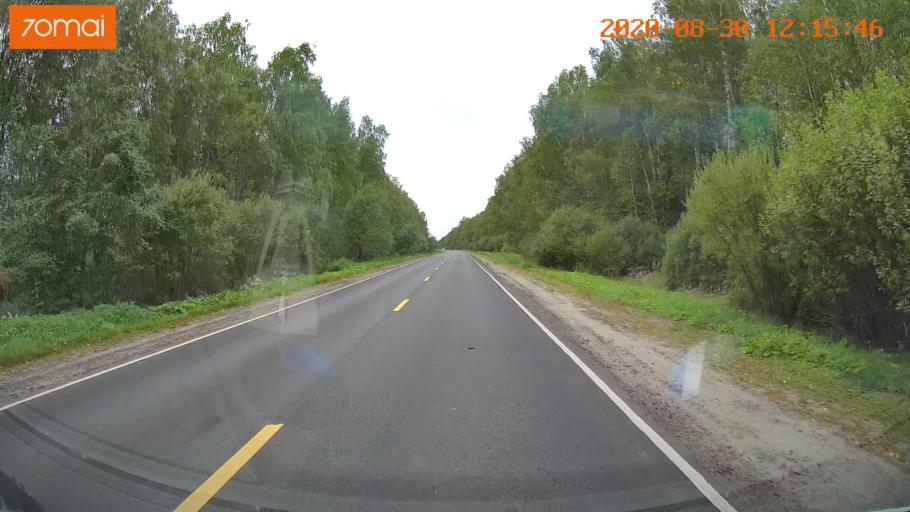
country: RU
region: Ivanovo
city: Yur'yevets
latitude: 57.3184
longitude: 43.0214
